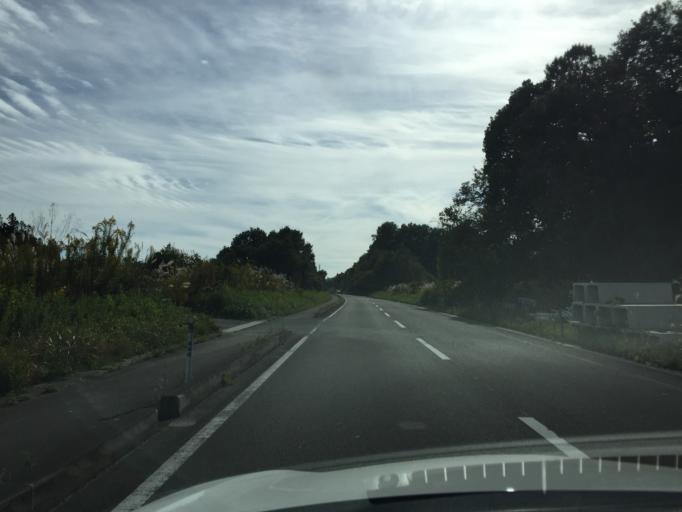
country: JP
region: Fukushima
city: Nihommatsu
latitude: 37.5645
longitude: 140.5010
